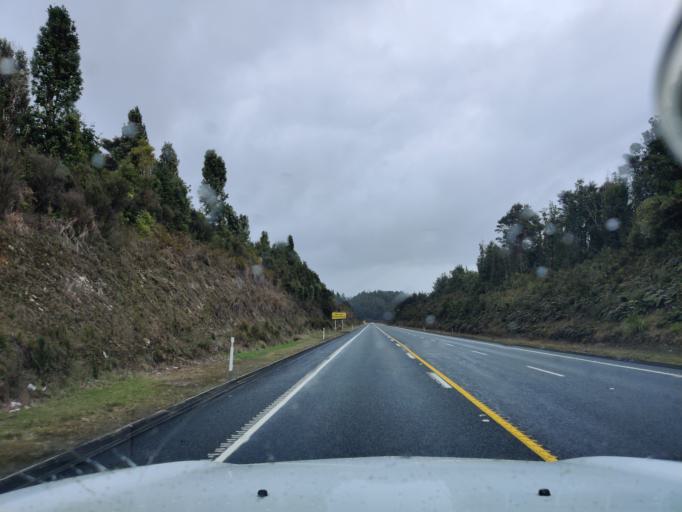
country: NZ
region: Waikato
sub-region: South Waikato District
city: Tokoroa
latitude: -38.0136
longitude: 175.9440
